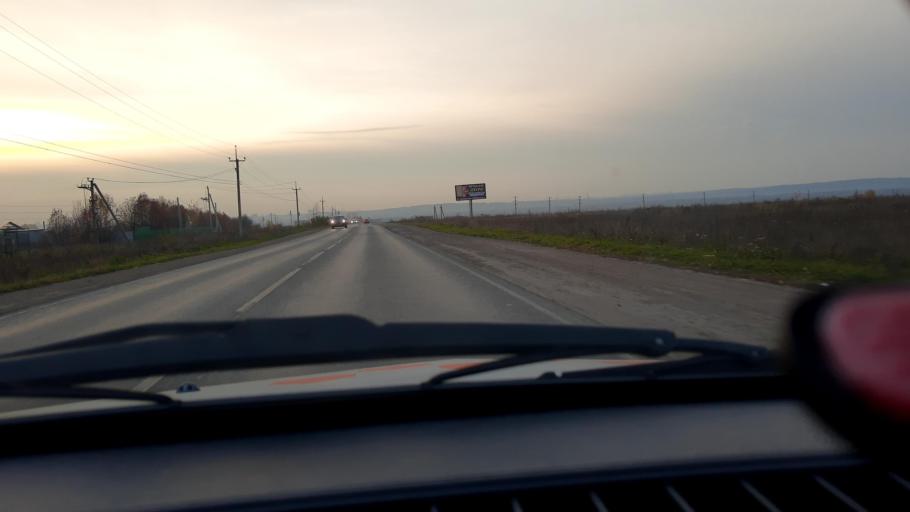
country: RU
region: Bashkortostan
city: Iglino
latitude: 54.7947
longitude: 56.2562
